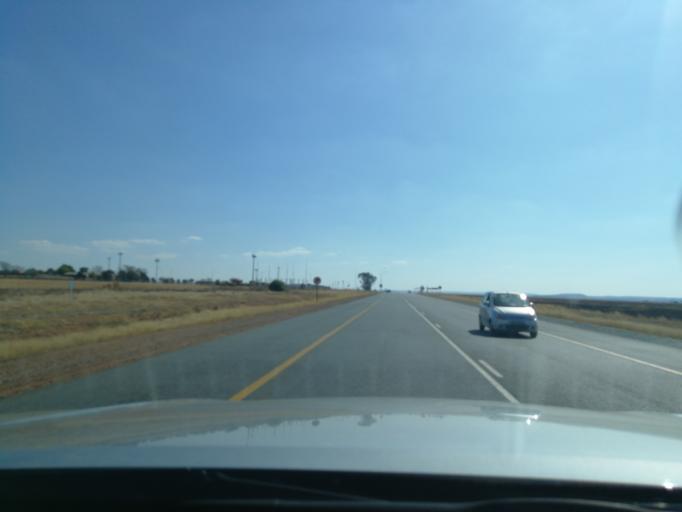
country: ZA
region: North-West
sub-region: Dr Kenneth Kaunda District Municipality
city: Klerksdorp
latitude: -26.8627
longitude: 26.5914
